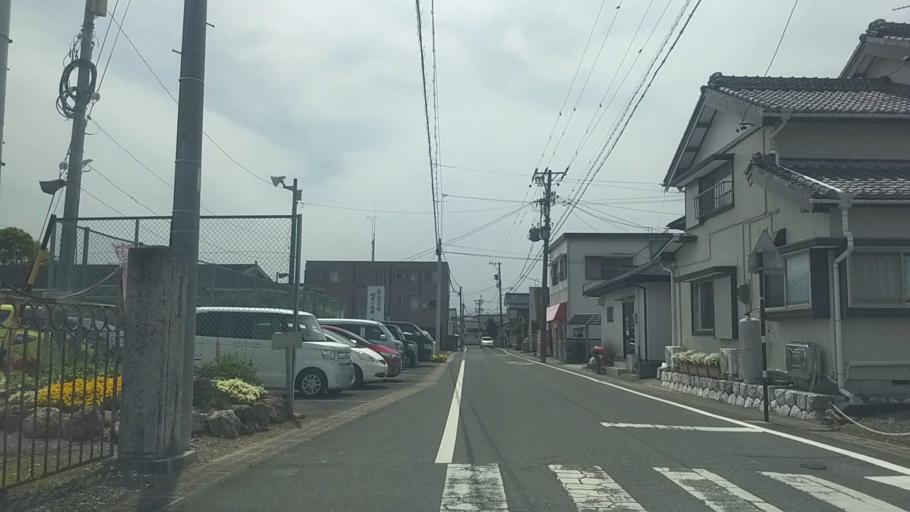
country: JP
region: Shizuoka
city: Kosai-shi
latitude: 34.7500
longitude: 137.5287
